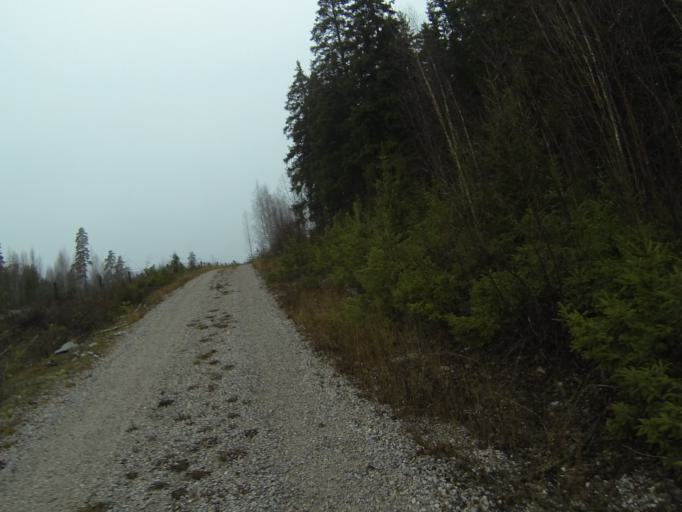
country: FI
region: Varsinais-Suomi
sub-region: Salo
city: Halikko
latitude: 60.4062
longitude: 22.9886
